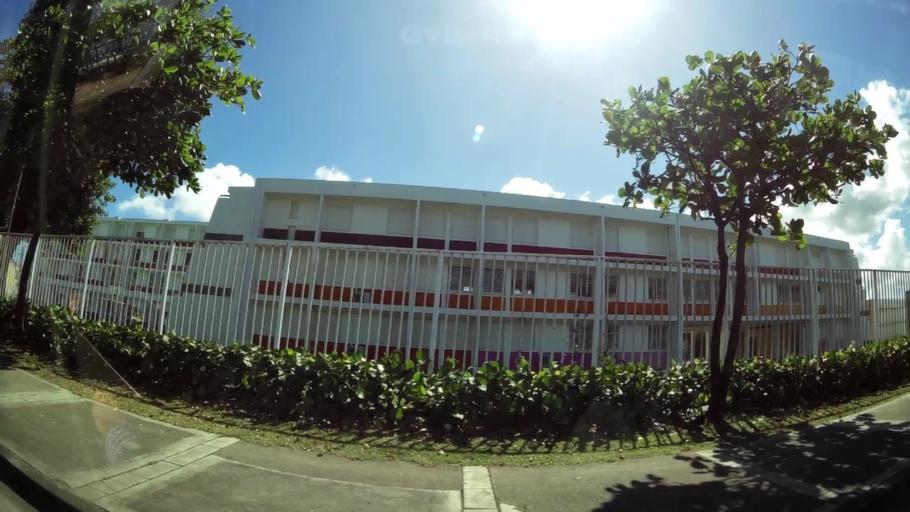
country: GP
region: Guadeloupe
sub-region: Guadeloupe
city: Le Moule
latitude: 16.3332
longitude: -61.3522
